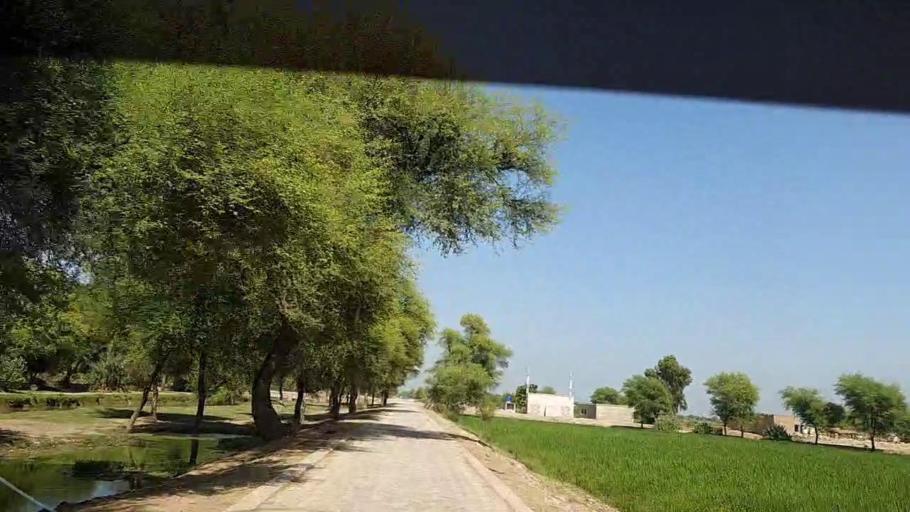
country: PK
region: Sindh
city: Kandhkot
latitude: 28.3023
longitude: 69.1095
